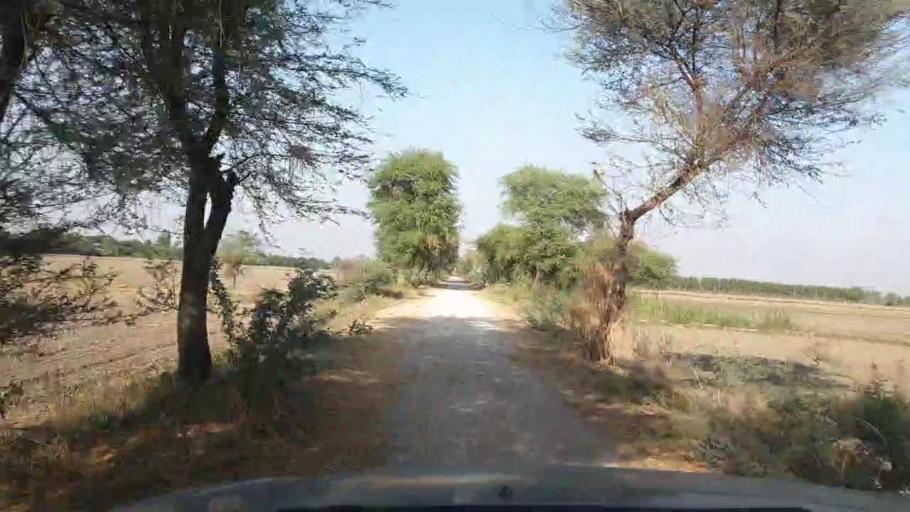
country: PK
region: Sindh
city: Tando Muhammad Khan
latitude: 25.0891
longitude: 68.5738
